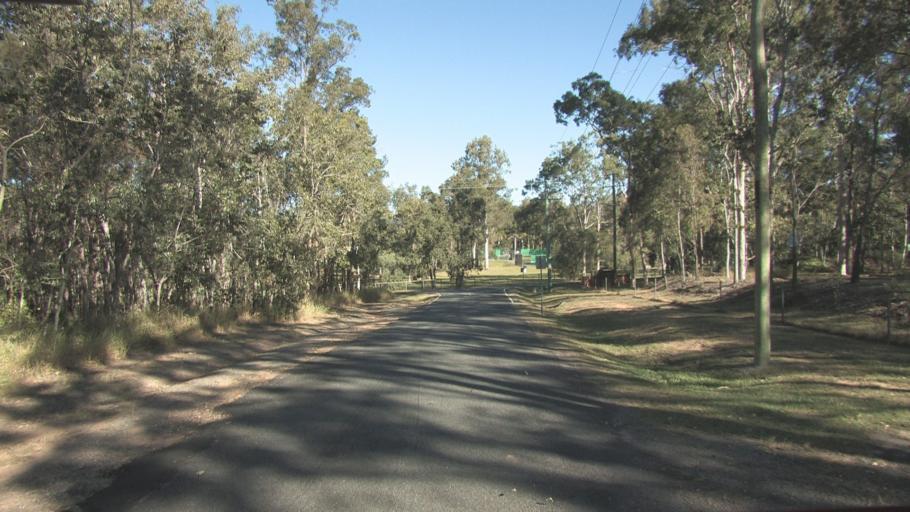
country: AU
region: Queensland
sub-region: Logan
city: Park Ridge South
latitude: -27.7227
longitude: 153.0186
